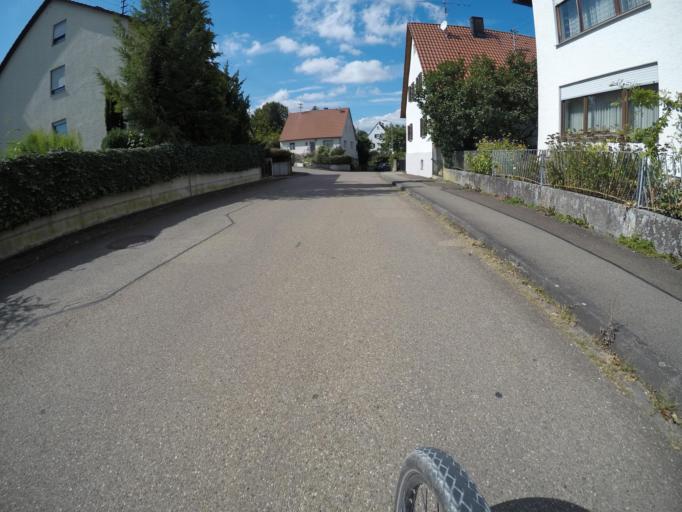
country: DE
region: Bavaria
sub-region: Swabia
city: Wittislingen
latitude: 48.6170
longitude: 10.4140
